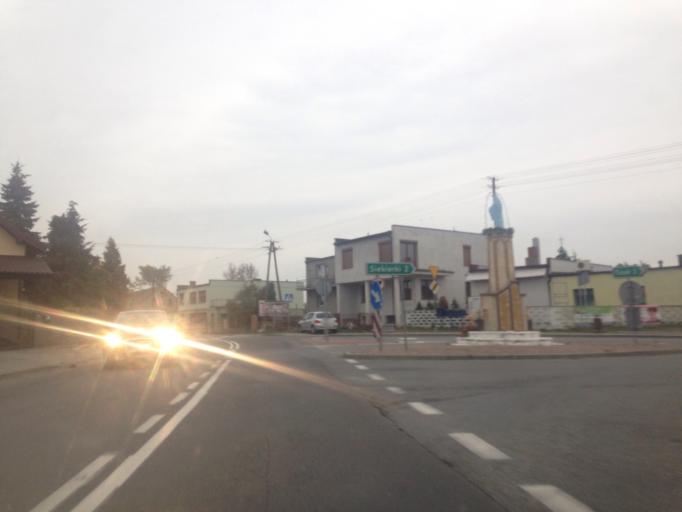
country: PL
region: Greater Poland Voivodeship
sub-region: Powiat poznanski
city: Kleszczewo
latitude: 52.3613
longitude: 17.1318
